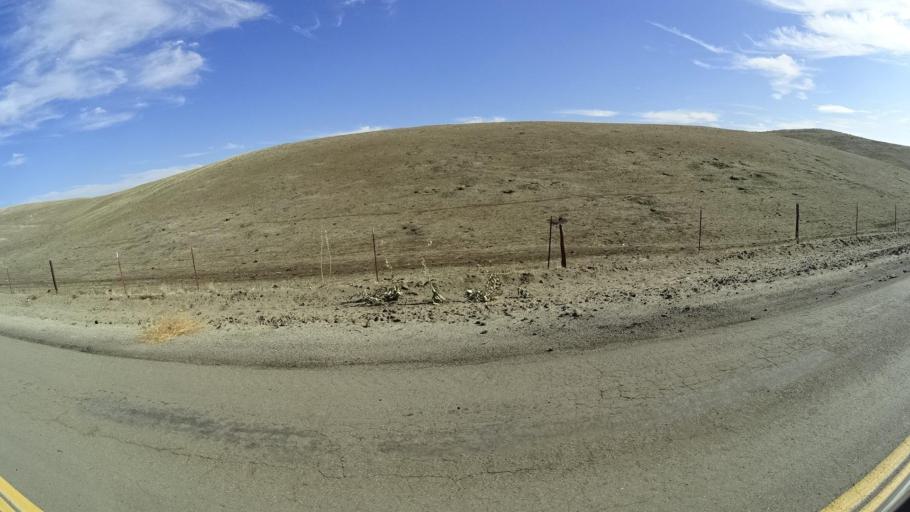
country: US
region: California
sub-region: Kern County
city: Oildale
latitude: 35.6110
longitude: -118.9444
